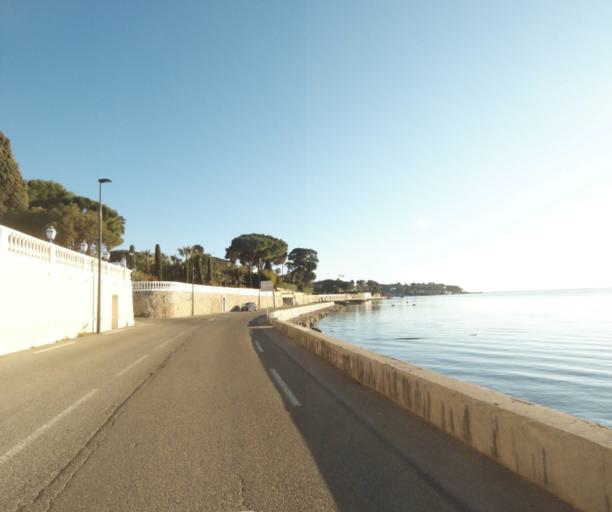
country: FR
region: Provence-Alpes-Cote d'Azur
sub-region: Departement des Alpes-Maritimes
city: Antibes
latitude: 43.5597
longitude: 7.1216
